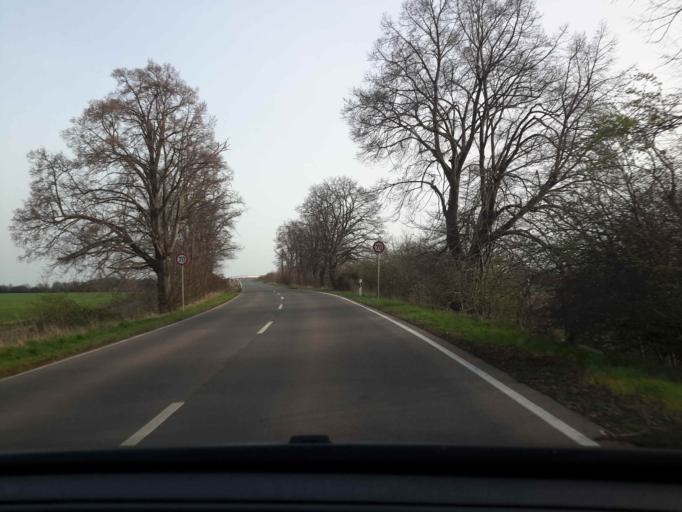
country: DE
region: Saxony
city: Rackwitz
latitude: 51.4144
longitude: 12.3601
